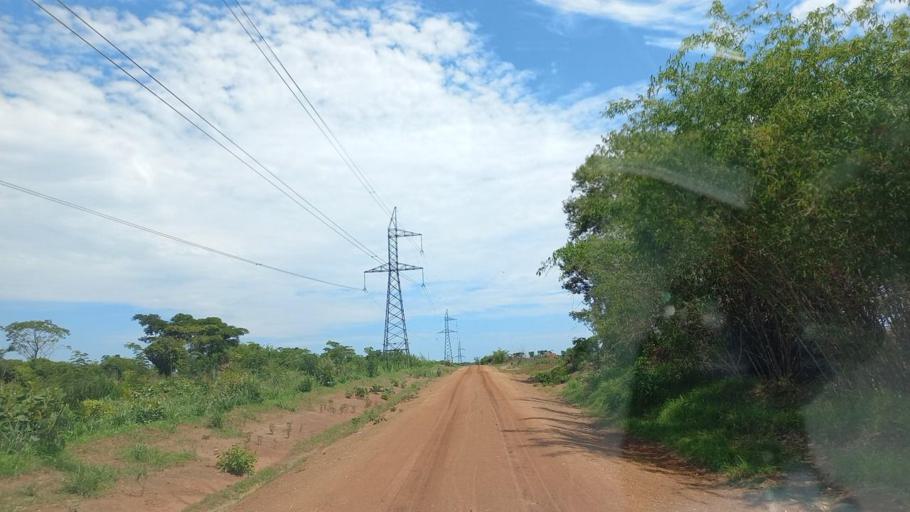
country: ZM
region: Copperbelt
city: Kitwe
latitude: -12.8208
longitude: 28.3530
